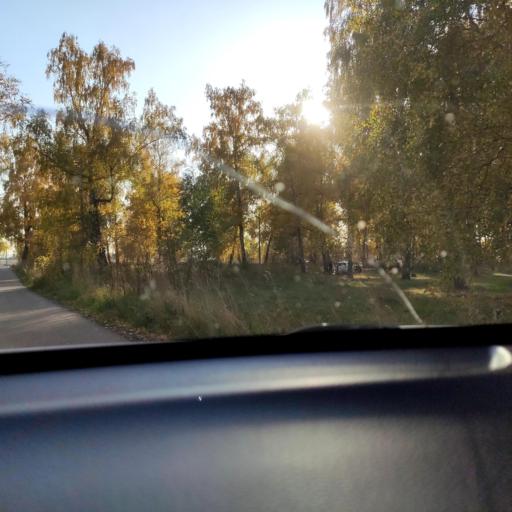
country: RU
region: Tatarstan
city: Stolbishchi
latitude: 55.7094
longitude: 49.1623
